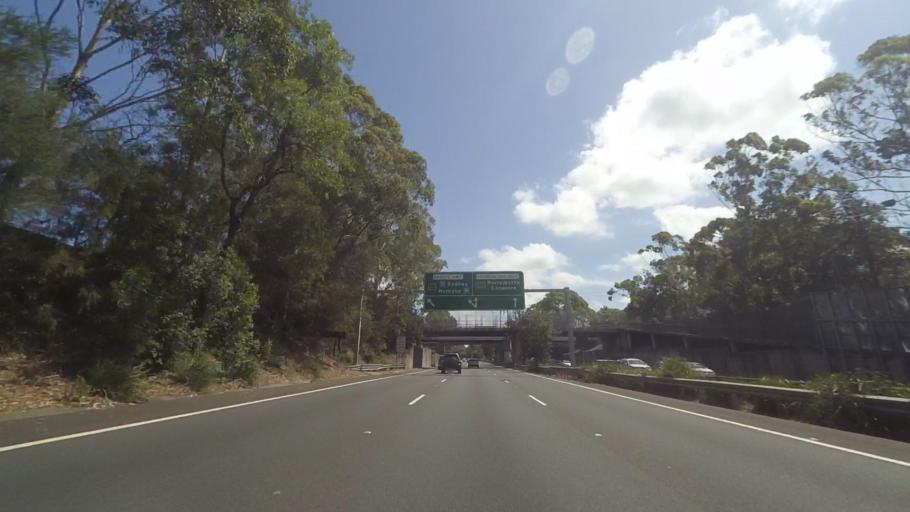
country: AU
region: New South Wales
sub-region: Ku-ring-gai
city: North Wahroonga
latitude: -33.7141
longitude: 151.1138
